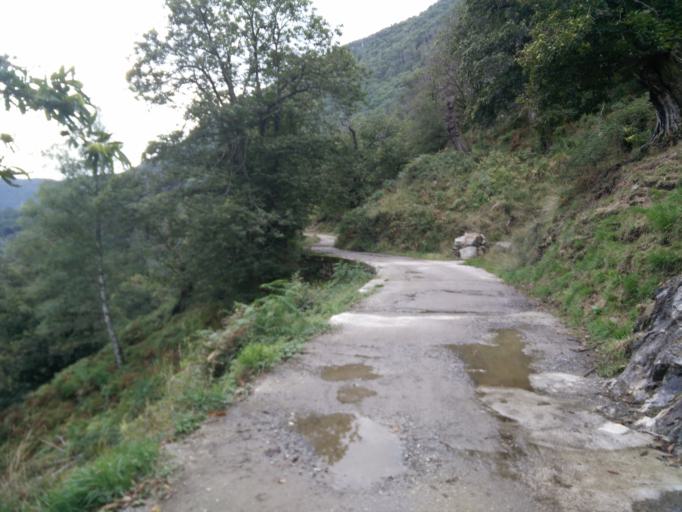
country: IT
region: Lombardy
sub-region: Provincia di Como
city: Livo
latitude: 46.1848
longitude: 9.3124
